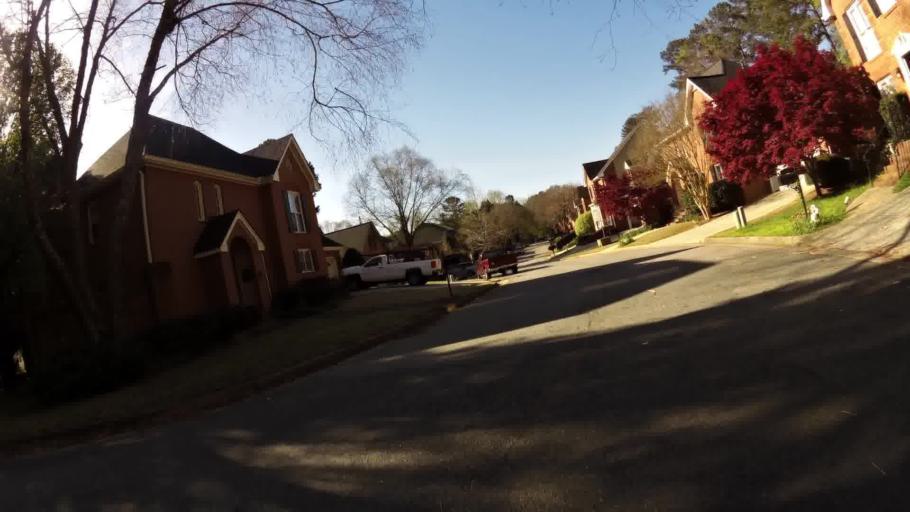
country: US
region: Georgia
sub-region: DeKalb County
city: Clarkston
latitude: 33.8323
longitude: -84.2684
